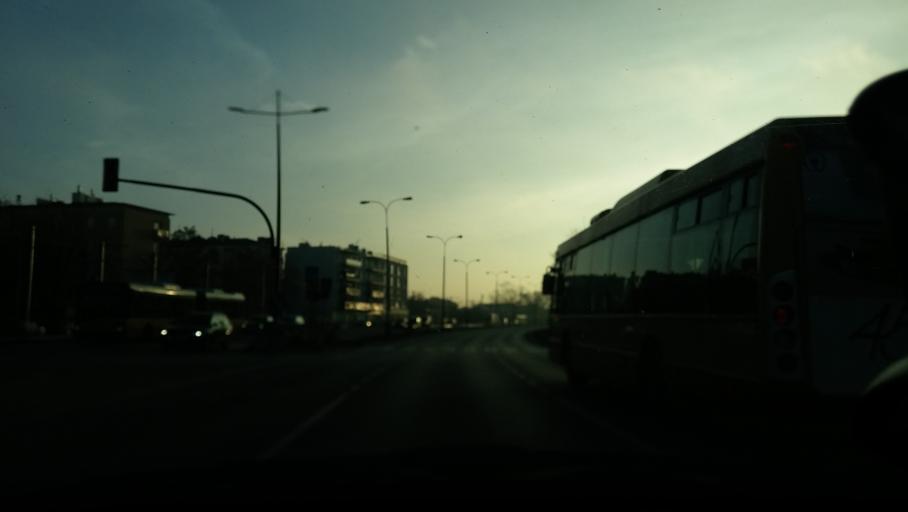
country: PL
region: Masovian Voivodeship
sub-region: Warszawa
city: Praga Poludnie
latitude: 52.2399
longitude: 21.1136
